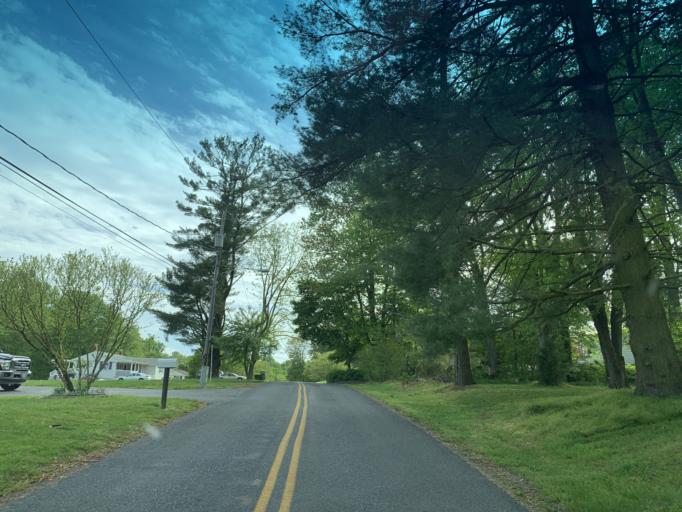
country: US
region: Maryland
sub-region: Harford County
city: Aberdeen
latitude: 39.6436
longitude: -76.2330
